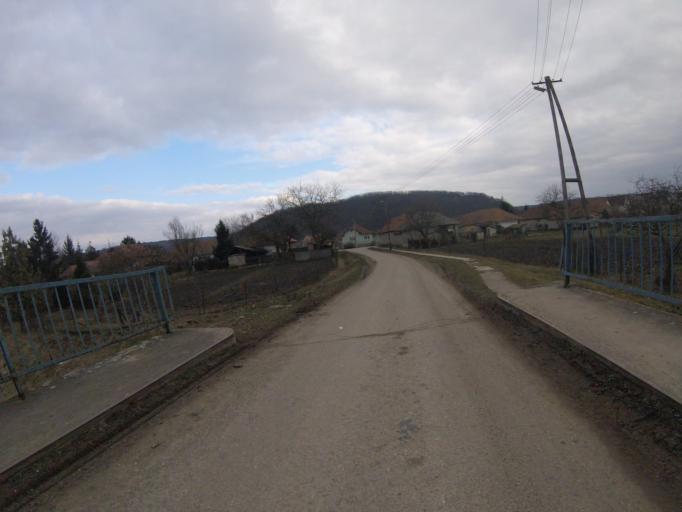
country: HU
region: Heves
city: Egerszalok
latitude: 47.8329
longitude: 20.3297
